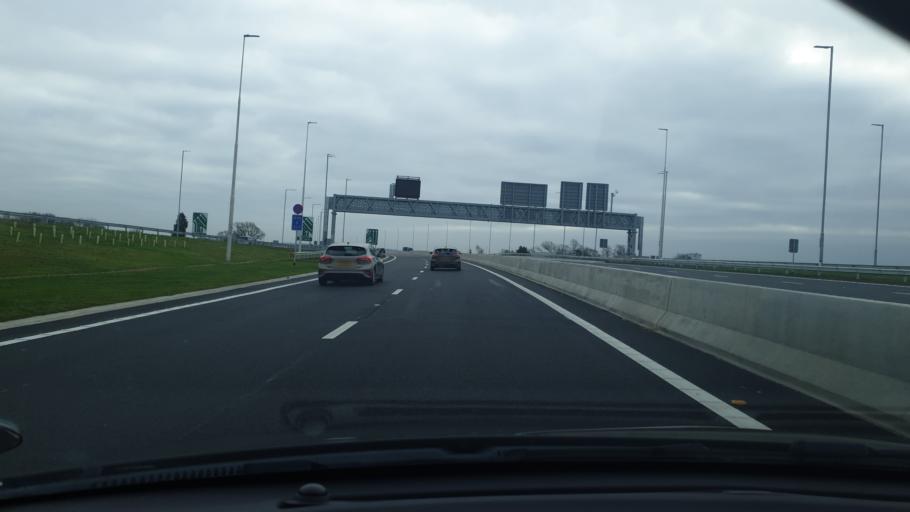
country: GB
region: England
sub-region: Cambridgeshire
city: Buckden
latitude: 52.3081
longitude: -0.2407
